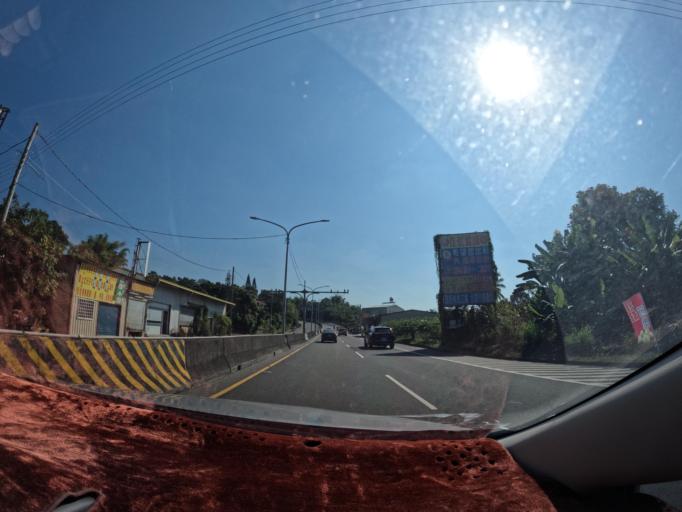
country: TW
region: Taiwan
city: Yujing
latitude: 23.0548
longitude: 120.4024
